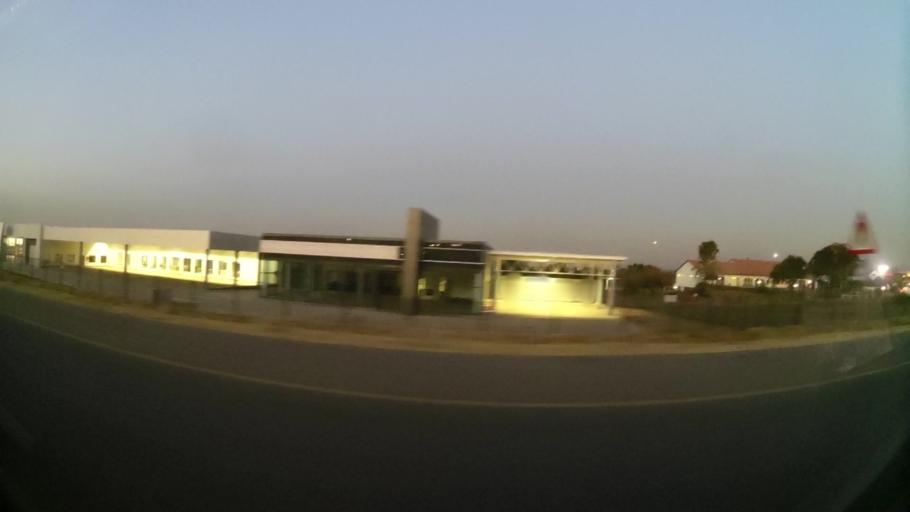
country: ZA
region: North-West
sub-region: Bojanala Platinum District Municipality
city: Rustenburg
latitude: -25.6874
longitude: 27.2538
